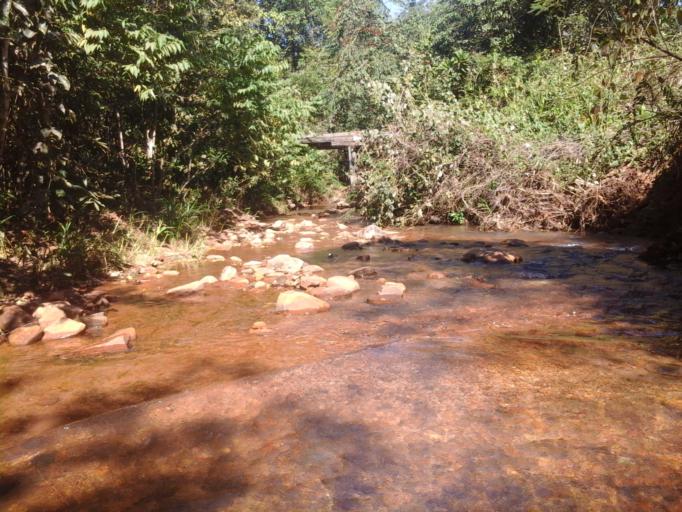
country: BR
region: Goias
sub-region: Pirenopolis
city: Pirenopolis
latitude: -15.8287
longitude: -49.1441
